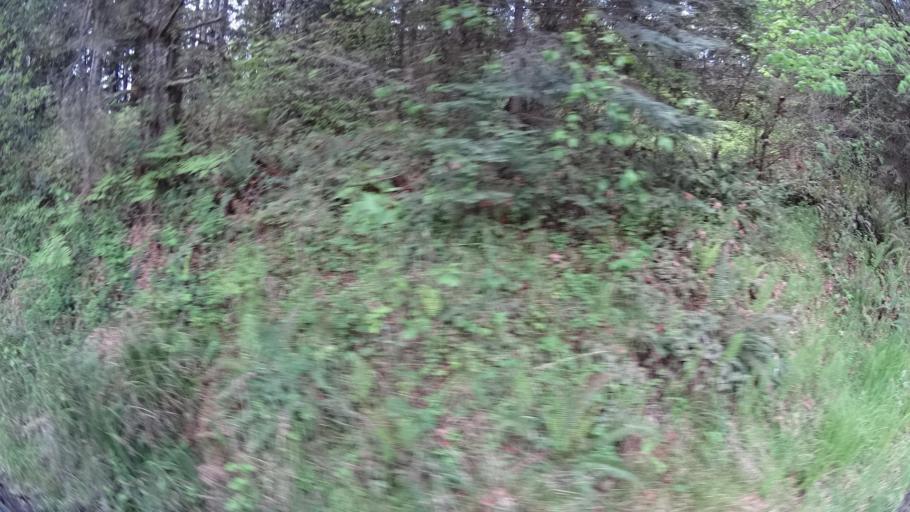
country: US
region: California
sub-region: Humboldt County
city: Blue Lake
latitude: 40.7848
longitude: -123.8800
